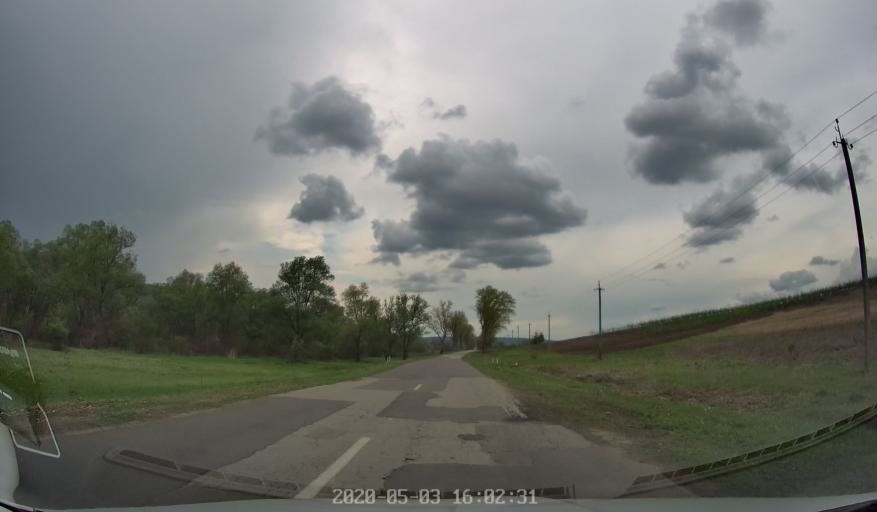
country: MD
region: Stinga Nistrului
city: Bucovat
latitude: 47.1736
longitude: 28.3944
